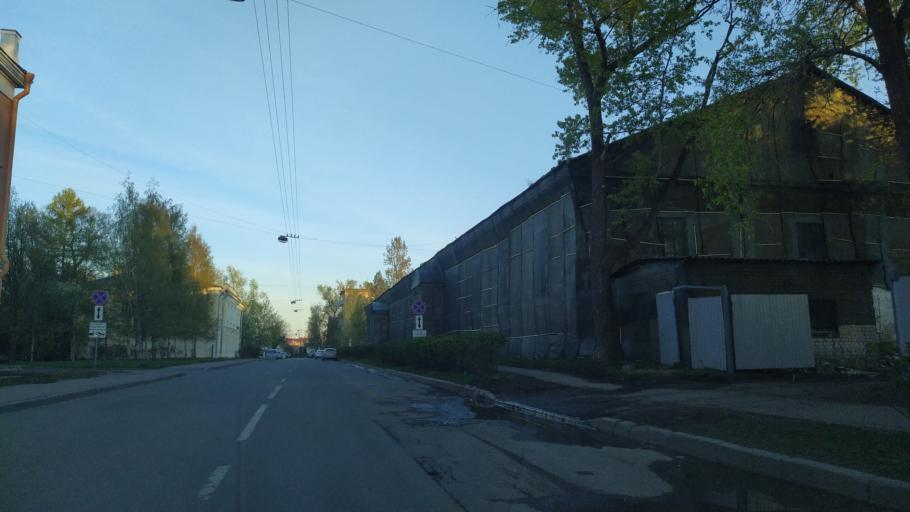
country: RU
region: St.-Petersburg
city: Pushkin
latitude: 59.7062
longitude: 30.4101
